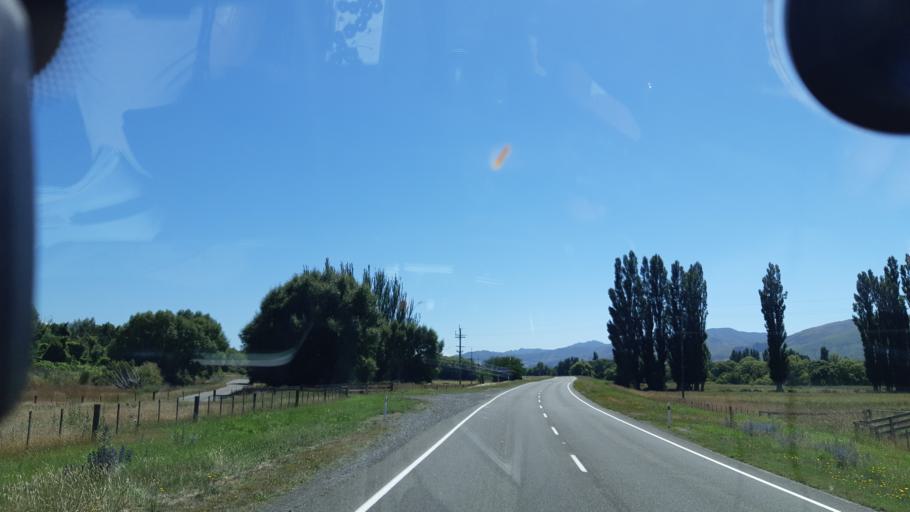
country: NZ
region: Canterbury
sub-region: Kaikoura District
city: Kaikoura
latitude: -42.7290
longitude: 173.2768
